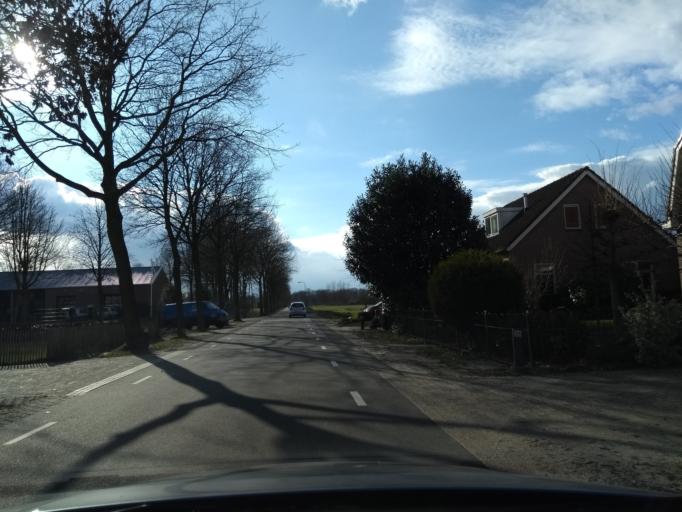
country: NL
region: Drenthe
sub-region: Gemeente De Wolden
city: Ruinen
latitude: 52.7193
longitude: 6.3012
